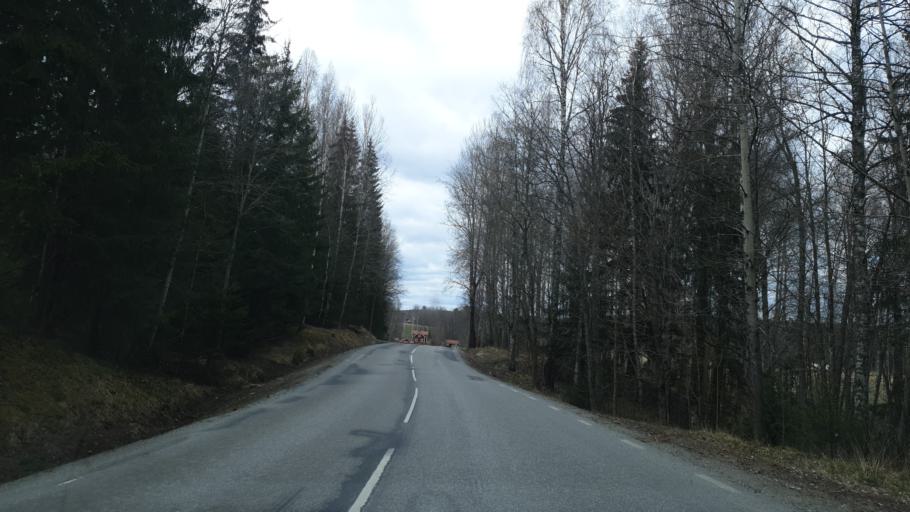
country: SE
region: OErebro
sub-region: Nora Kommun
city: Nora
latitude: 59.5478
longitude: 15.0294
